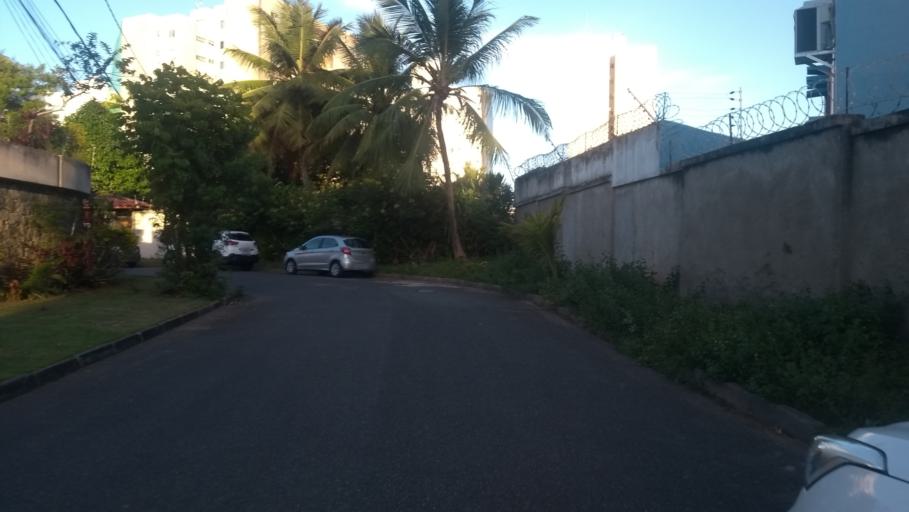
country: BR
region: Bahia
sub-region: Salvador
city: Salvador
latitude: -12.9906
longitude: -38.4632
